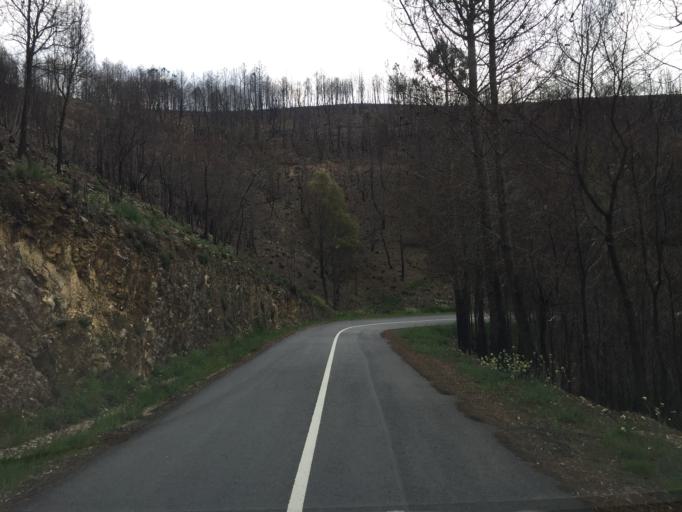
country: PT
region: Coimbra
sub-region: Arganil
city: Arganil
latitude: 40.1827
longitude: -7.9717
